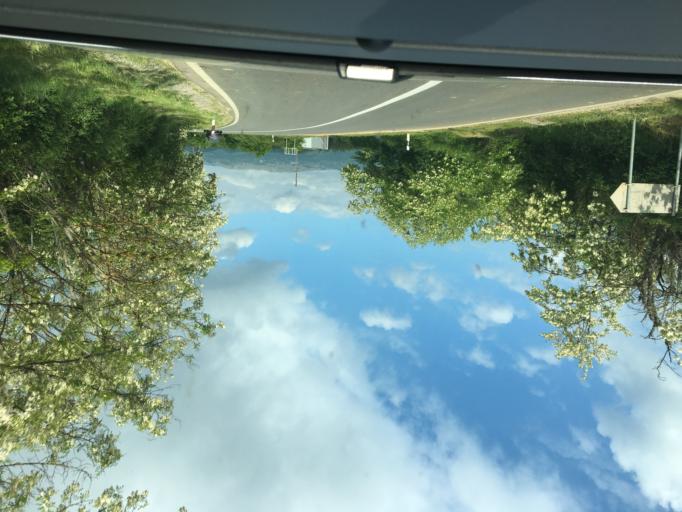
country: MK
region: Resen
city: Resen
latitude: 41.0703
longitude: 21.0370
